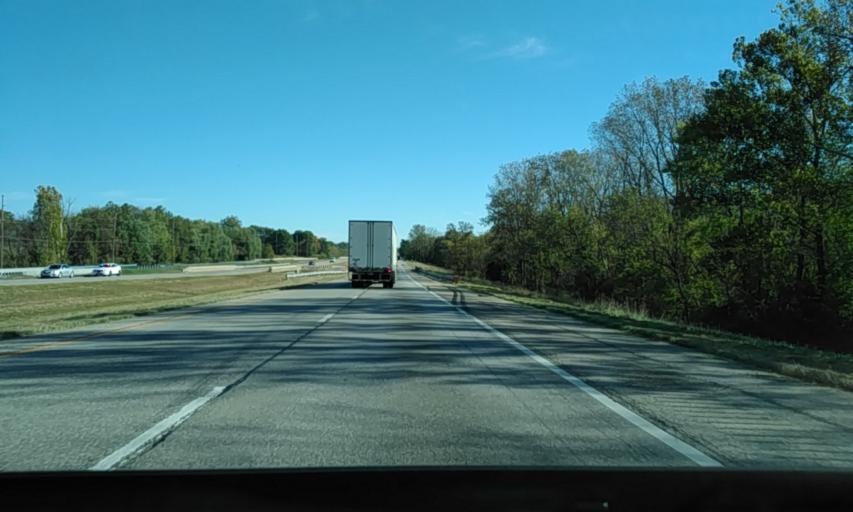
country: US
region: Illinois
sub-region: Bond County
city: Greenville
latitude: 38.8342
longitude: -89.5098
